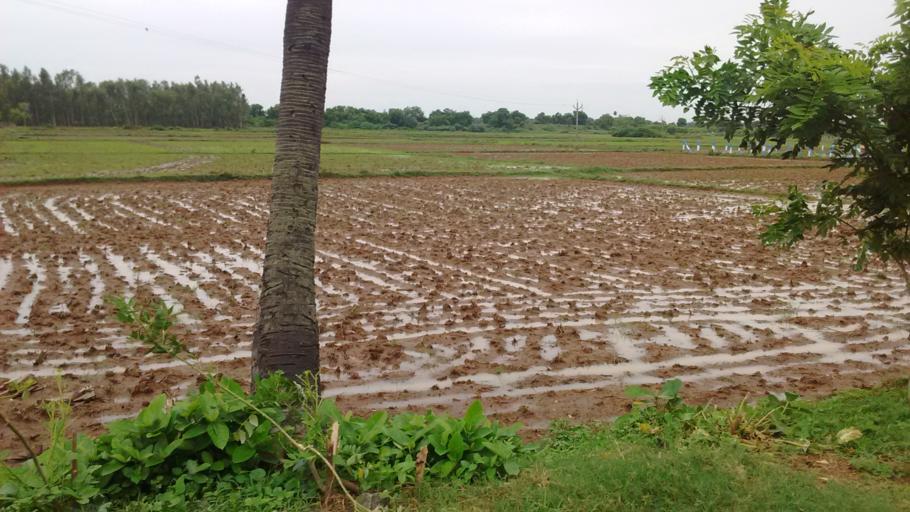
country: IN
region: Tamil Nadu
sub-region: Kancheepuram
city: Madambakkam
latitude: 12.9162
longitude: 80.0018
